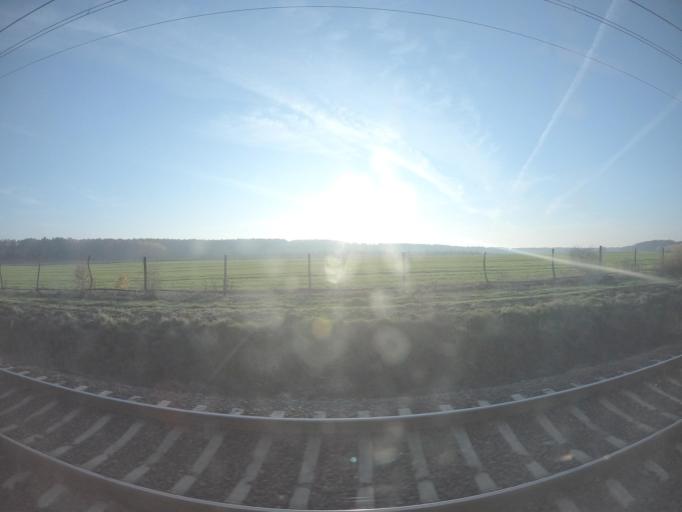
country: PL
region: Lubusz
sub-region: Powiat slubicki
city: Rzepin
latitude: 52.2784
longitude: 14.9082
